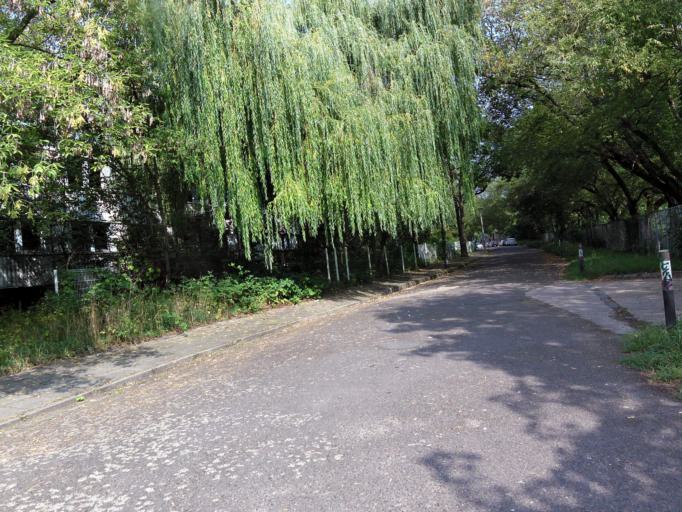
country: DE
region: Saxony
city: Leipzig
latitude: 51.3727
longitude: 12.3479
